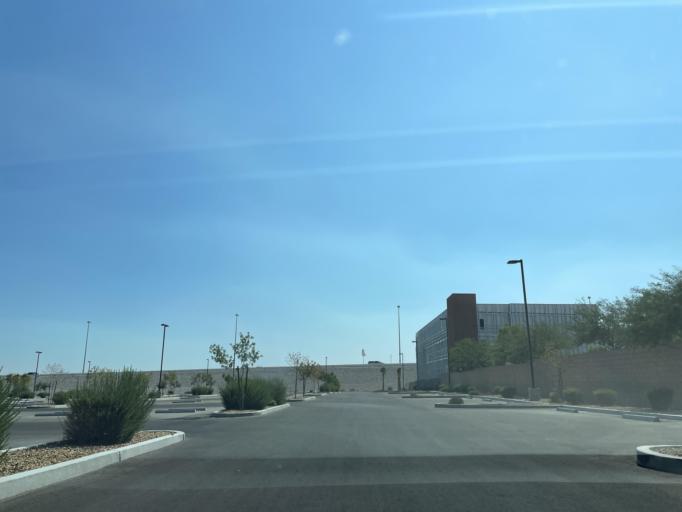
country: US
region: Nevada
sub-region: Clark County
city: Summerlin South
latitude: 36.2804
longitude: -115.2821
